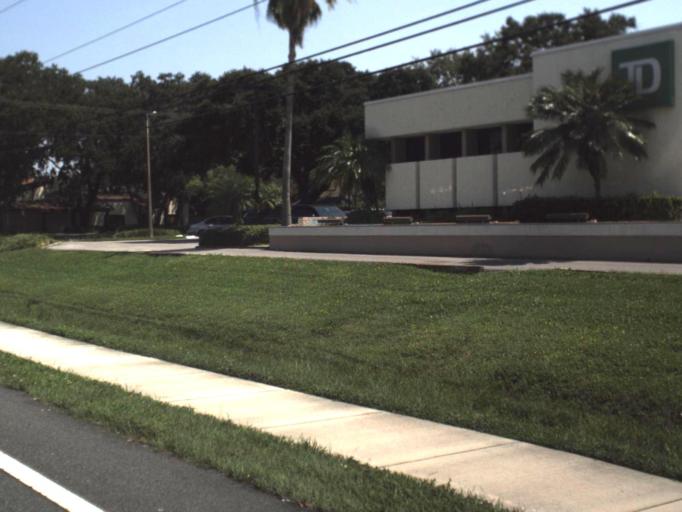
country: US
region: Florida
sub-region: Hillsborough County
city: Carrollwood
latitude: 28.0468
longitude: -82.5044
